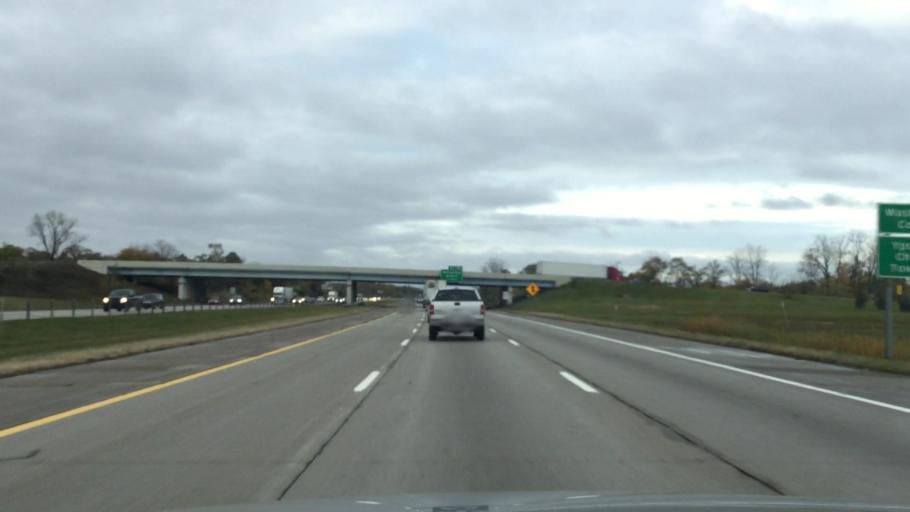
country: US
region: Michigan
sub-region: Wayne County
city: Belleville
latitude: 42.2188
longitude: -83.5435
